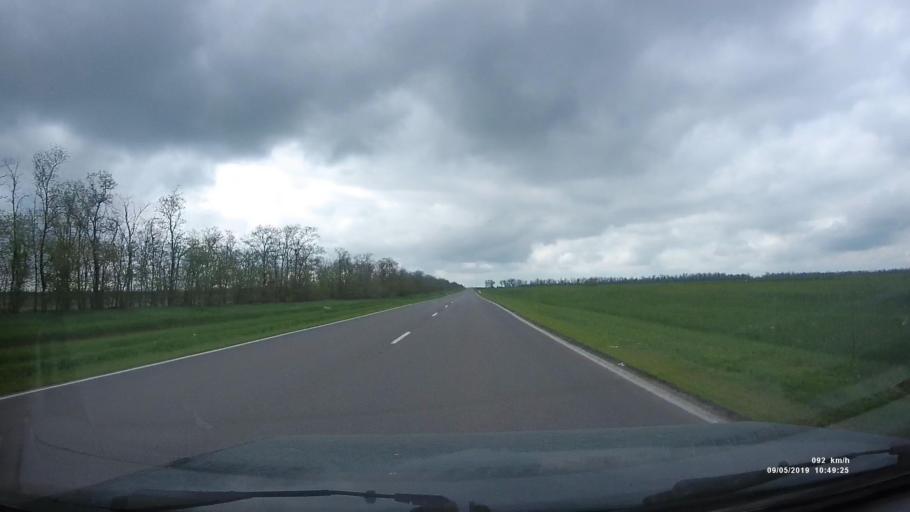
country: RU
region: Rostov
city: Peshkovo
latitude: 46.9430
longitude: 39.3559
